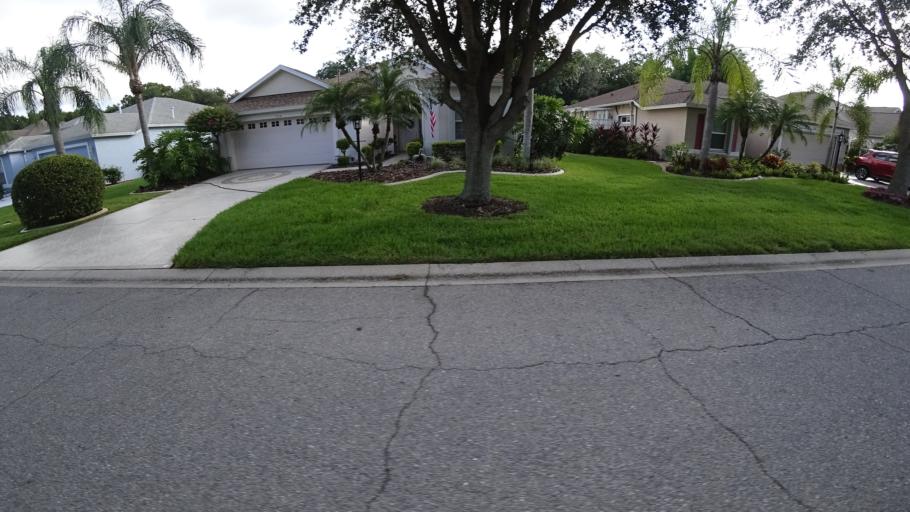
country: US
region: Florida
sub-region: Sarasota County
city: Desoto Lakes
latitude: 27.4231
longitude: -82.4946
